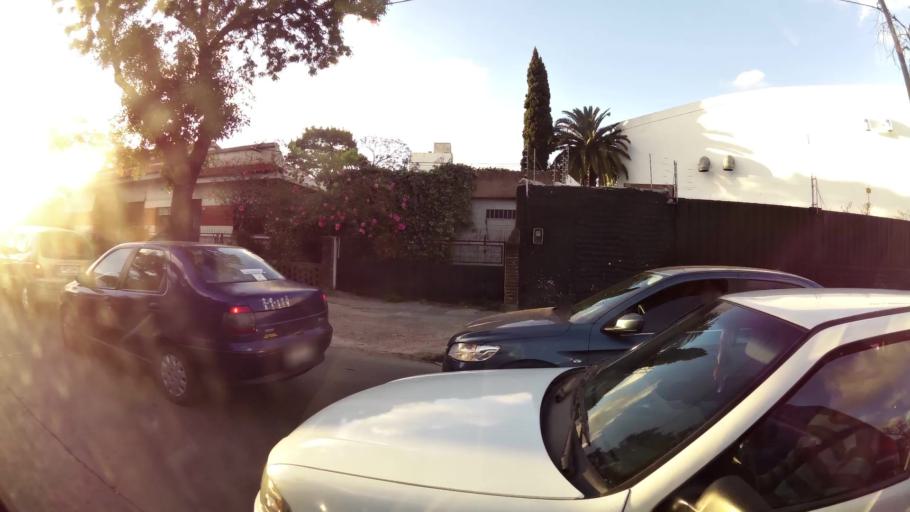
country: UY
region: Montevideo
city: Montevideo
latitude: -34.8809
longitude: -56.1530
